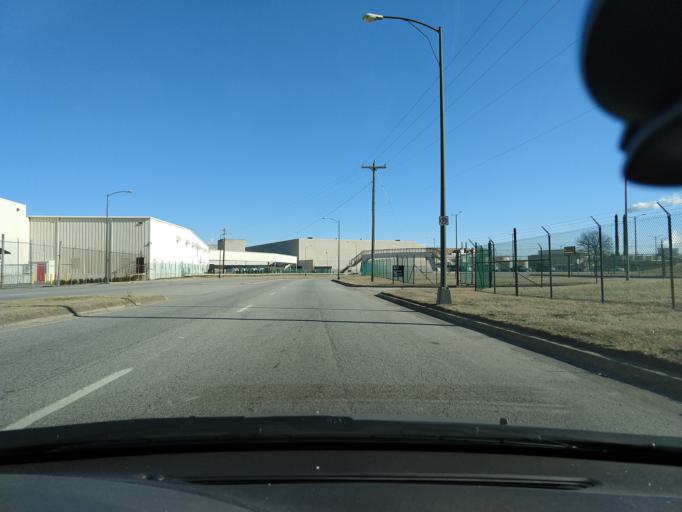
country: US
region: Virginia
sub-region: Chesterfield County
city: Bensley
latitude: 37.4724
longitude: -77.4374
